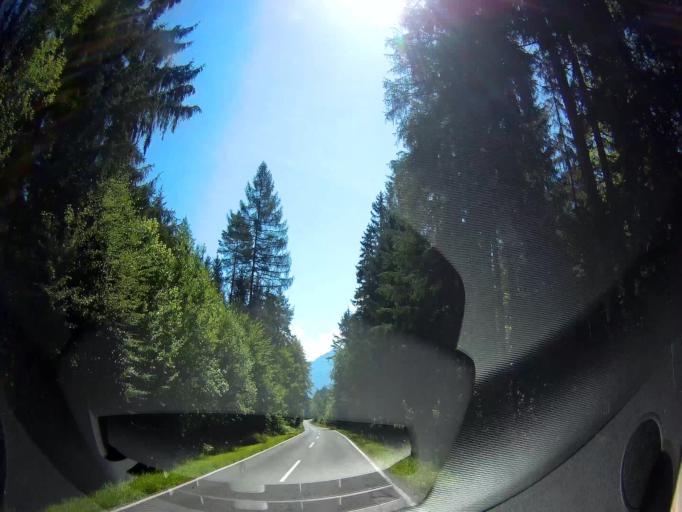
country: AT
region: Carinthia
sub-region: Politischer Bezirk Volkermarkt
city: Gallizien
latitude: 46.5427
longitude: 14.5453
